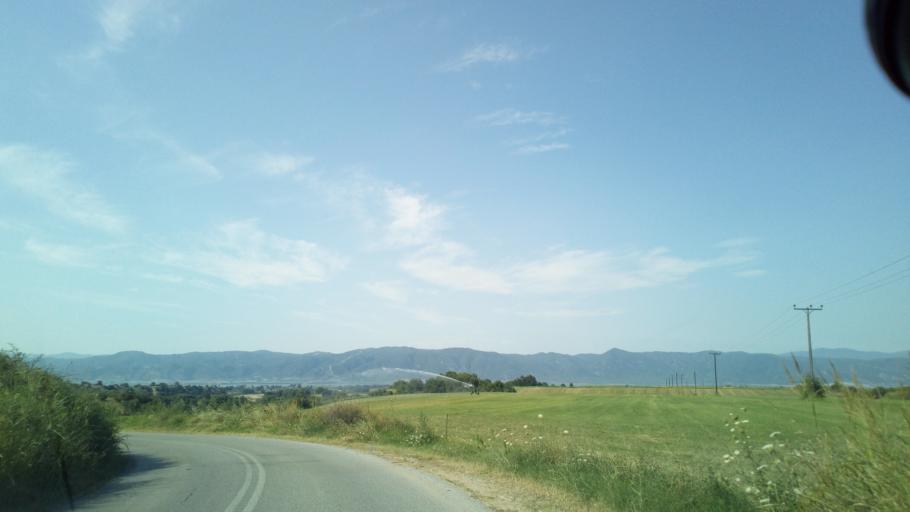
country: GR
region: Central Macedonia
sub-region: Nomos Thessalonikis
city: Nea Apollonia
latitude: 40.6146
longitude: 23.4606
